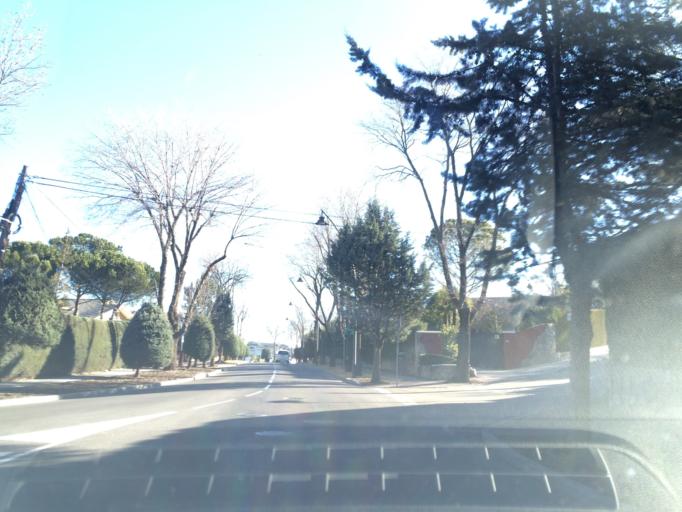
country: ES
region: Madrid
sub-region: Provincia de Madrid
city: Tres Cantos
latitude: 40.6116
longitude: -3.6915
